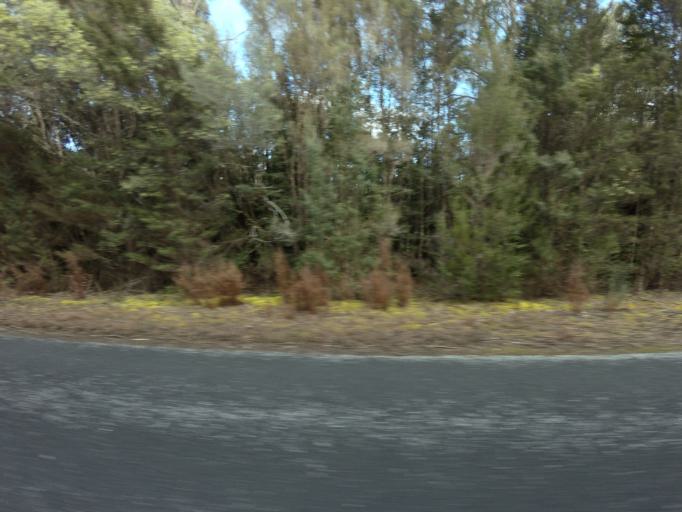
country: AU
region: Tasmania
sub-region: West Coast
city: Queenstown
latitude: -42.8030
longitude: 146.0960
